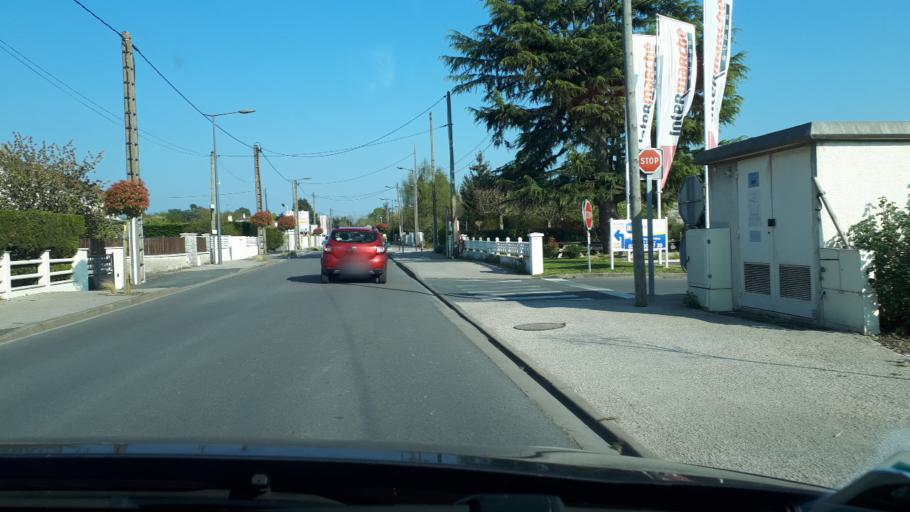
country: FR
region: Centre
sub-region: Departement d'Indre-et-Loire
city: Blere
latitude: 47.3252
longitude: 1.0051
